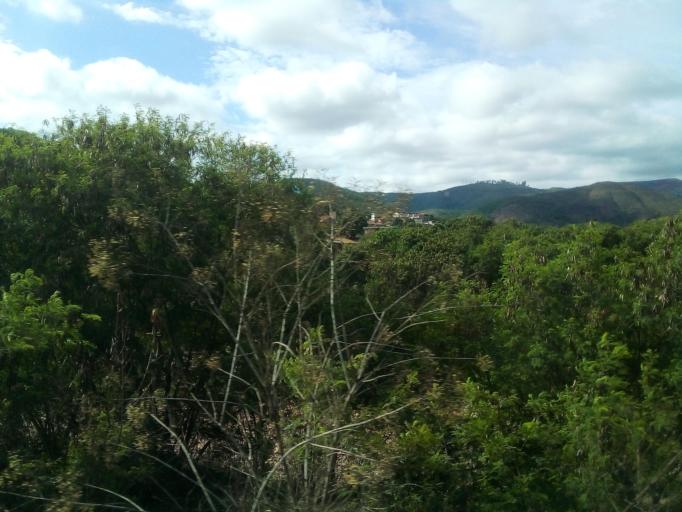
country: BR
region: Minas Gerais
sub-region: Belo Horizonte
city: Belo Horizonte
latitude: -19.8839
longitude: -43.8619
